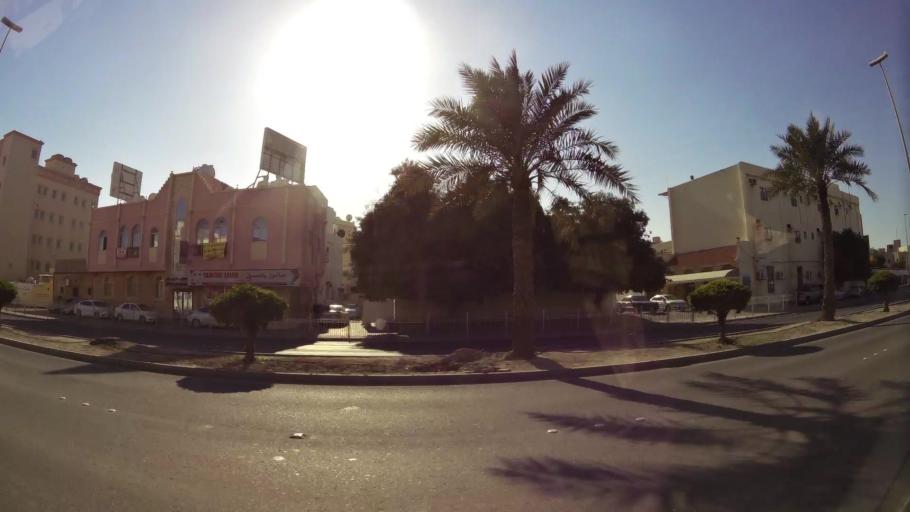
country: BH
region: Manama
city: Manama
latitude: 26.2135
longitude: 50.5659
